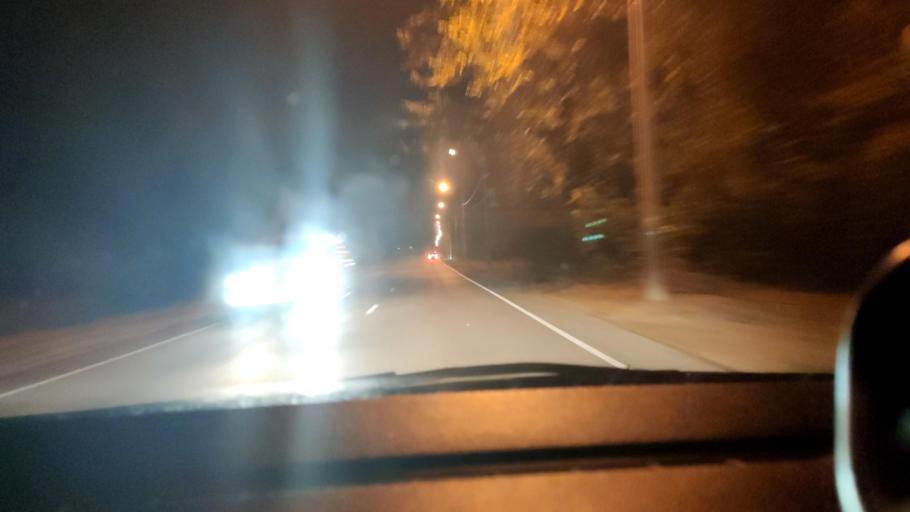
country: RU
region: Voronezj
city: Pridonskoy
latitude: 51.6115
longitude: 39.0500
